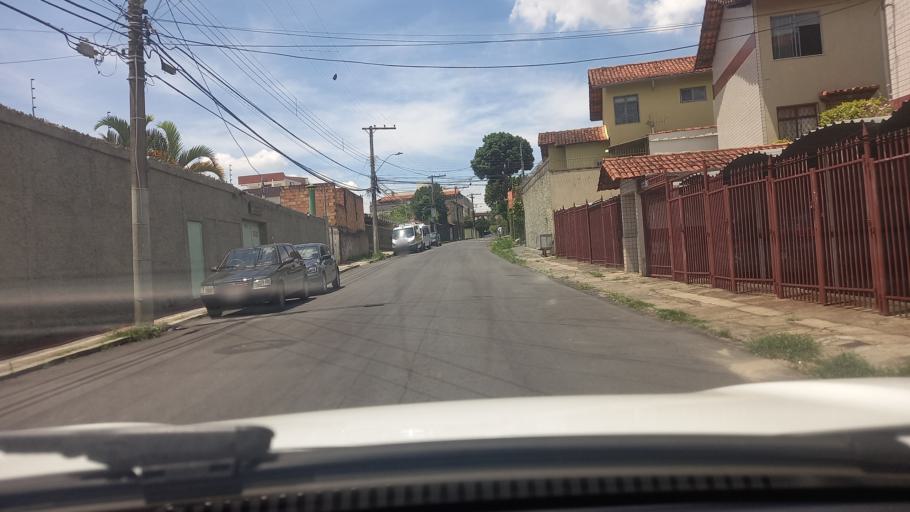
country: BR
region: Minas Gerais
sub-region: Belo Horizonte
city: Belo Horizonte
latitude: -19.9188
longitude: -43.9861
